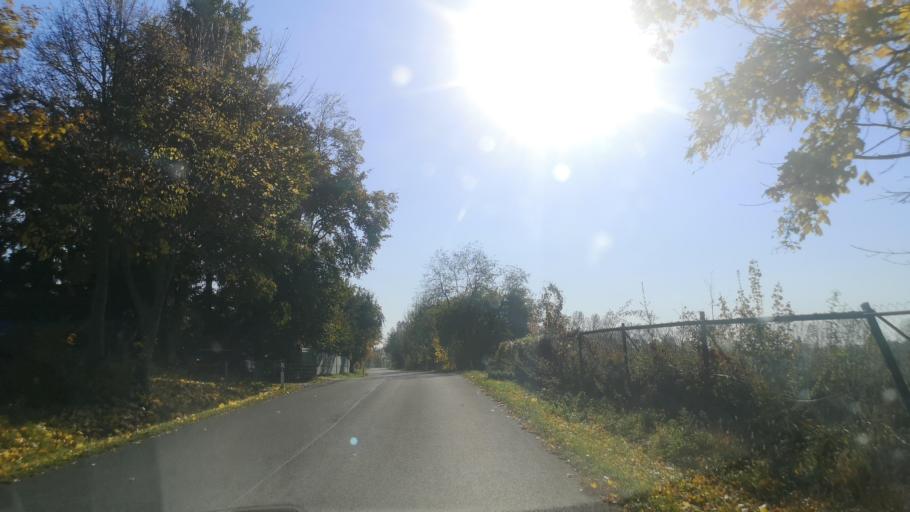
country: SK
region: Nitriansky
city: Zlate Moravce
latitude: 48.4263
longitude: 18.4244
